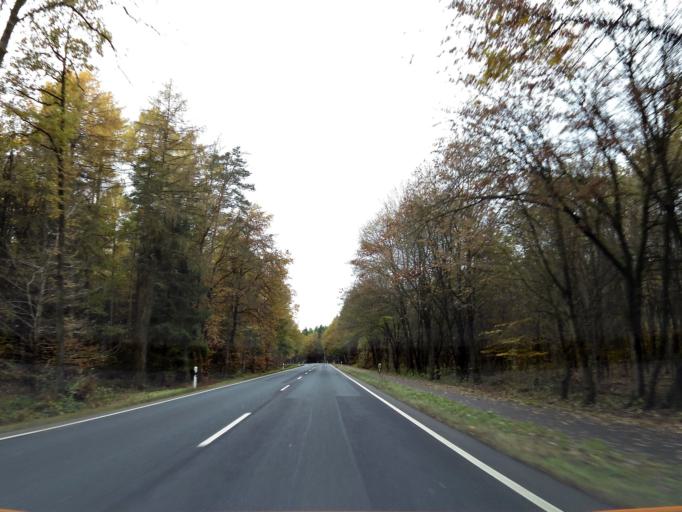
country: DE
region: Lower Saxony
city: Uelzen
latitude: 52.9525
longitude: 10.5104
